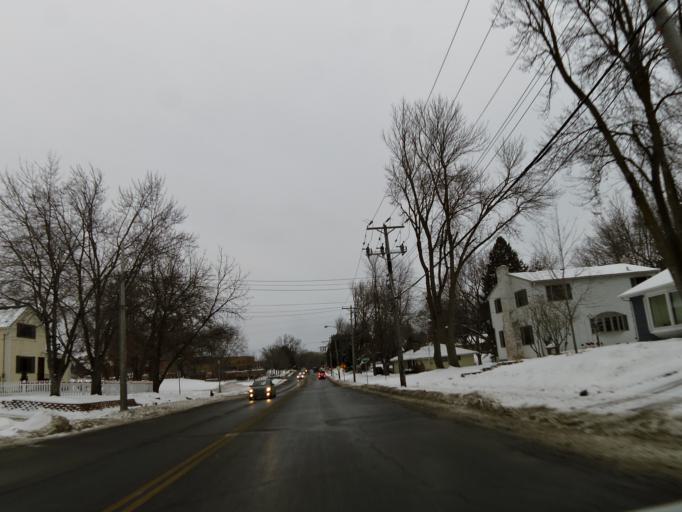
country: US
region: Minnesota
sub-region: Washington County
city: Stillwater
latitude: 45.0497
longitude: -92.8193
